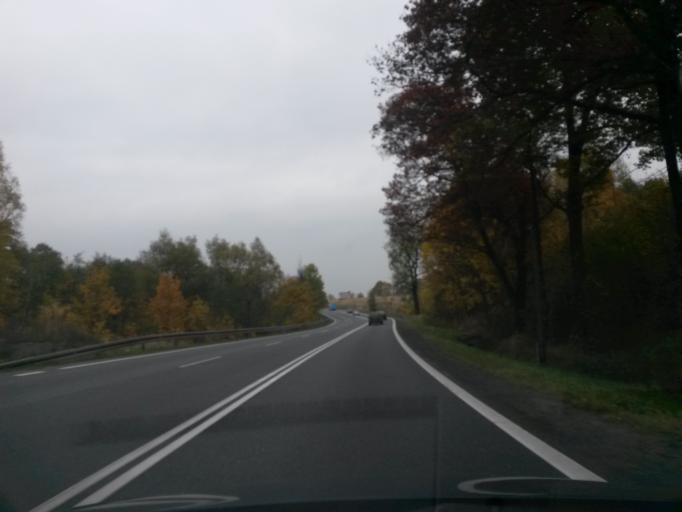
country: PL
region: Lower Silesian Voivodeship
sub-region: Powiat zabkowicki
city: Bardo
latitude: 50.4941
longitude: 16.7224
